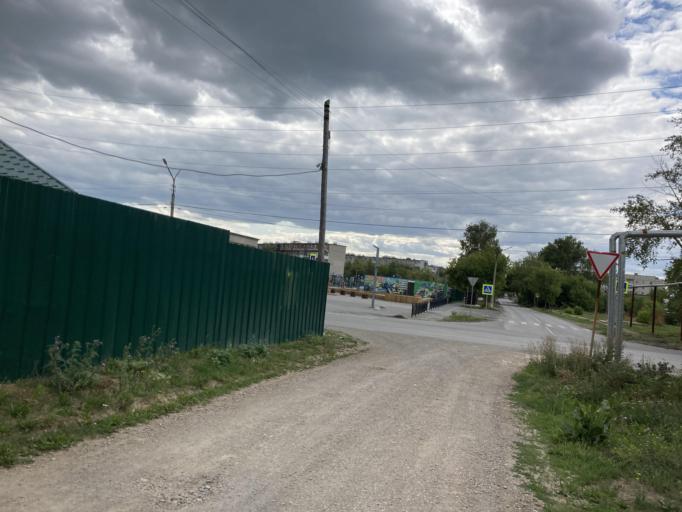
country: RU
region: Sverdlovsk
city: Bogdanovich
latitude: 56.7891
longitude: 62.0462
